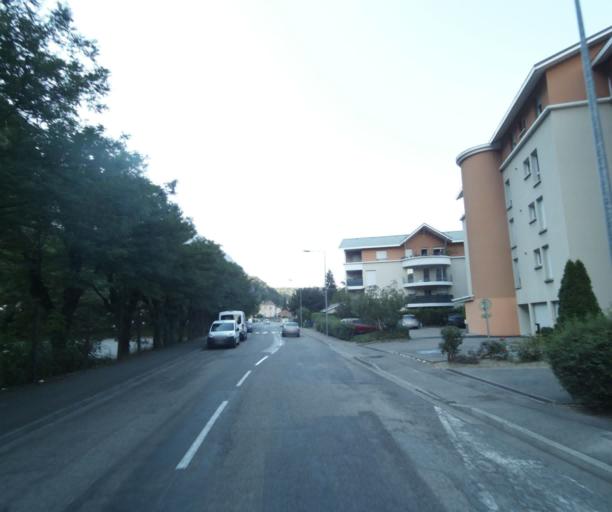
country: FR
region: Rhone-Alpes
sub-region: Departement de l'Isere
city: Sassenage
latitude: 45.2046
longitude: 5.6613
